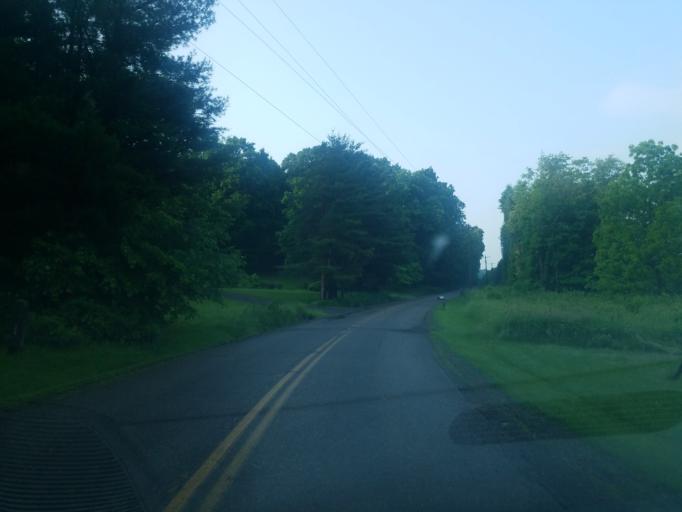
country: US
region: Ohio
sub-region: Stark County
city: Minerva
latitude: 40.6738
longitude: -81.1080
